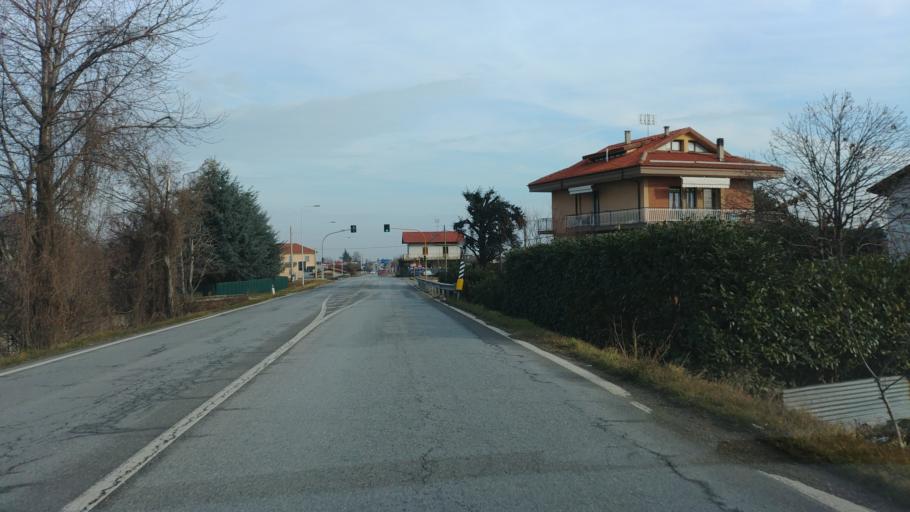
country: IT
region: Piedmont
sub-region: Provincia di Cuneo
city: Cuneo
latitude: 44.3777
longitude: 7.5566
